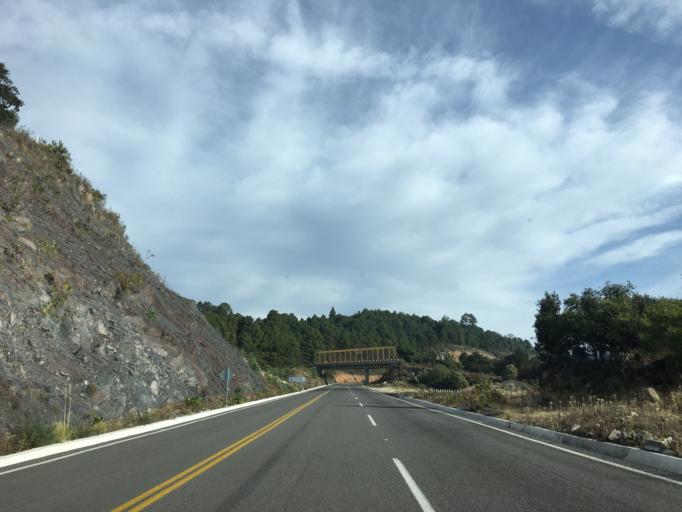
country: MX
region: Mexico
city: San Bartolo
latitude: 19.2615
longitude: -100.0651
